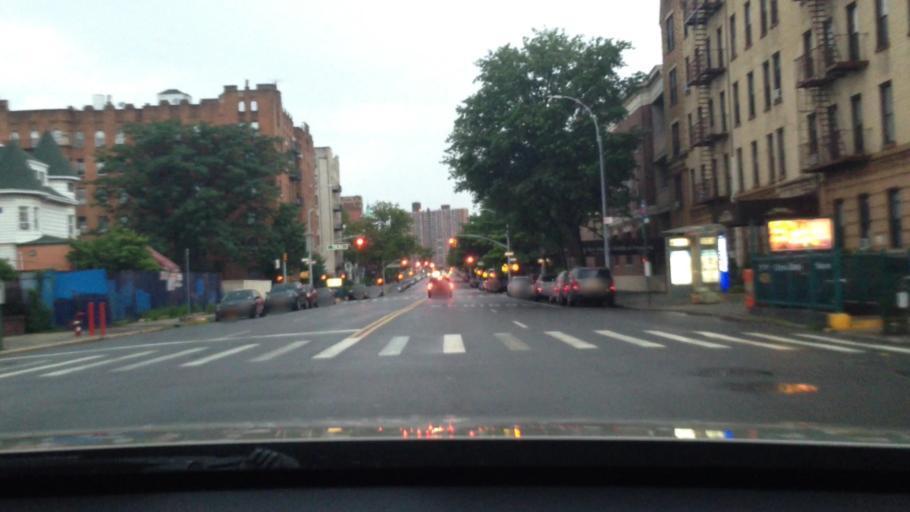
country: US
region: New York
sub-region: Kings County
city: Bensonhurst
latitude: 40.6291
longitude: -74.0257
